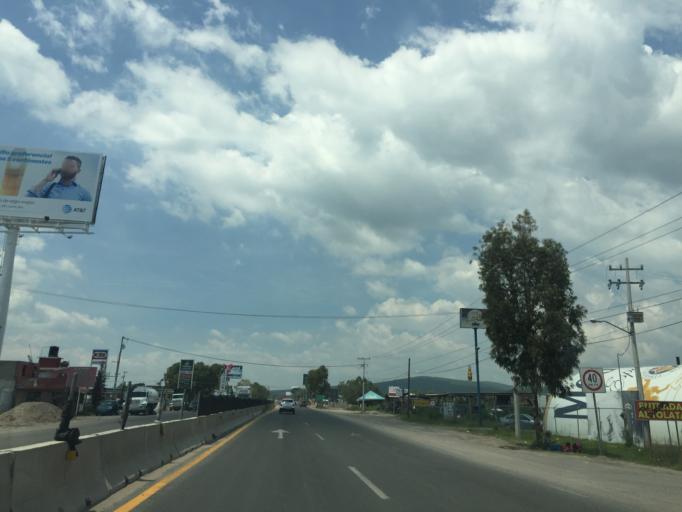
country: MX
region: Guanajuato
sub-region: Leon
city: Fraccionamiento Paseo de las Torres
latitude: 21.1836
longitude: -101.7440
